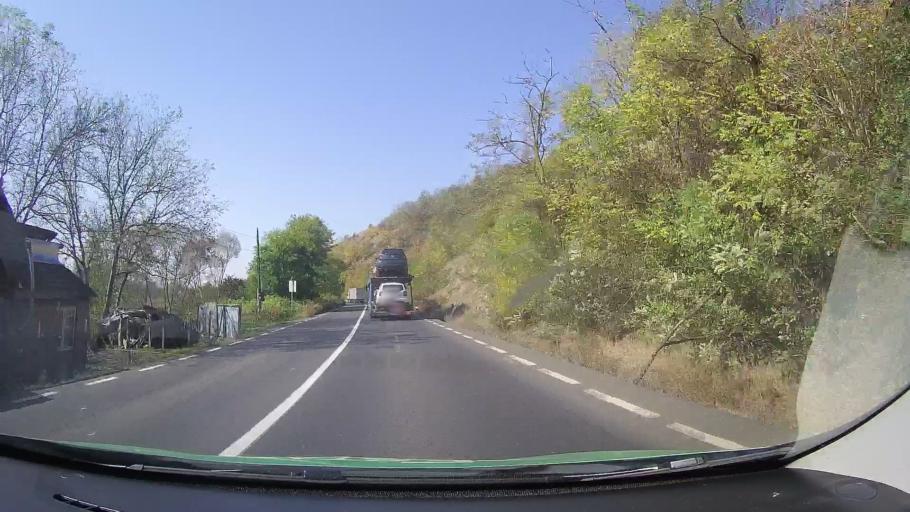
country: RO
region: Arad
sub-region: Comuna Varadia de Mures
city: Varadia de Mures
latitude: 46.0340
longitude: 22.1004
